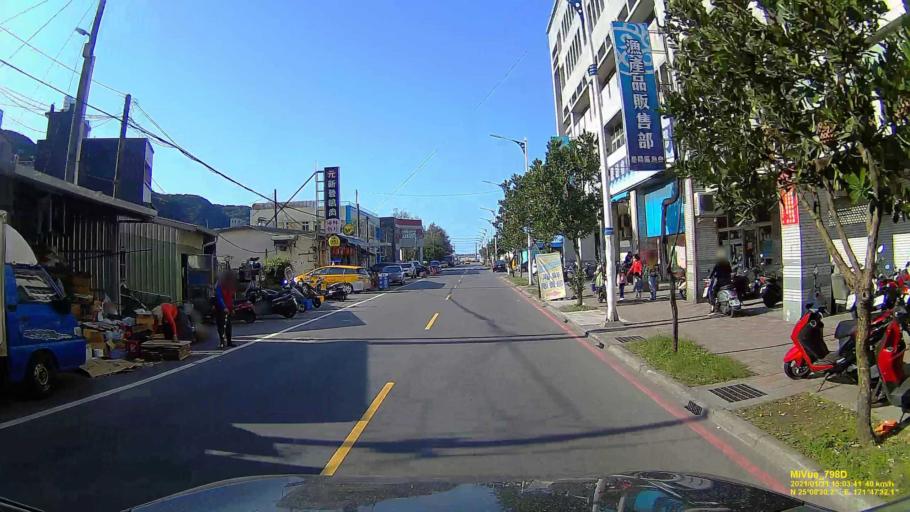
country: TW
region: Taiwan
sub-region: Keelung
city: Keelung
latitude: 25.1417
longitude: 121.7923
